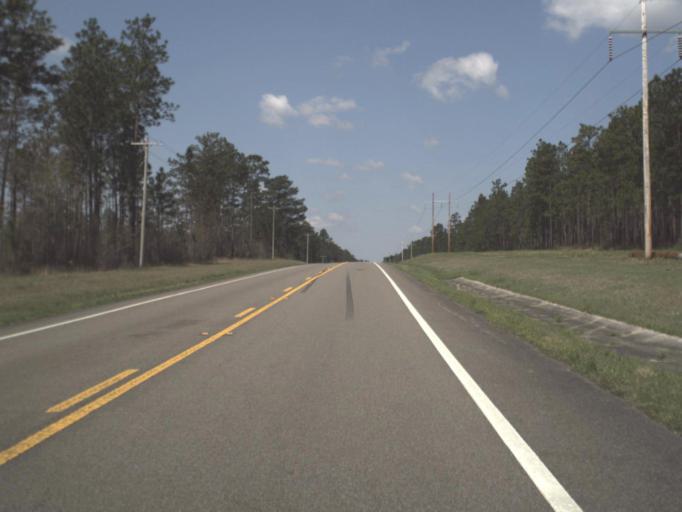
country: US
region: Florida
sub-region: Santa Rosa County
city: Point Baker
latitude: 30.8664
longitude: -86.9153
